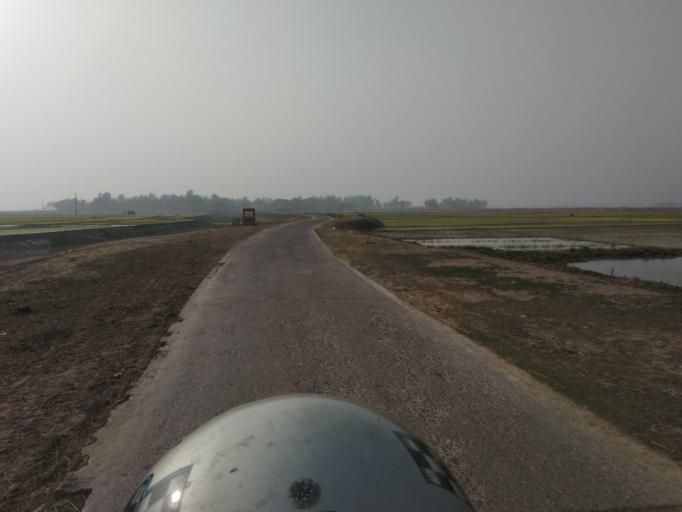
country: BD
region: Rajshahi
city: Ishurdi
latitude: 24.4876
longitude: 89.2088
